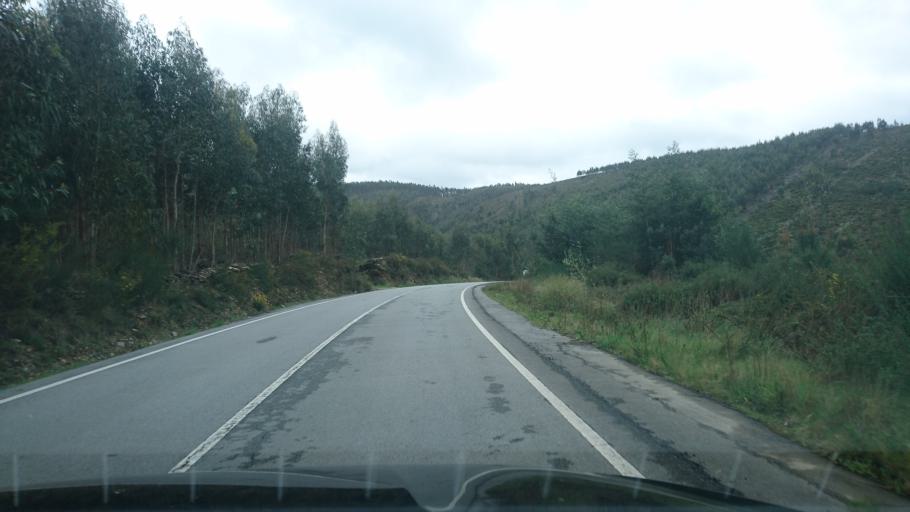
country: PT
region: Porto
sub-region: Paredes
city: Recarei
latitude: 41.1323
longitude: -8.3998
